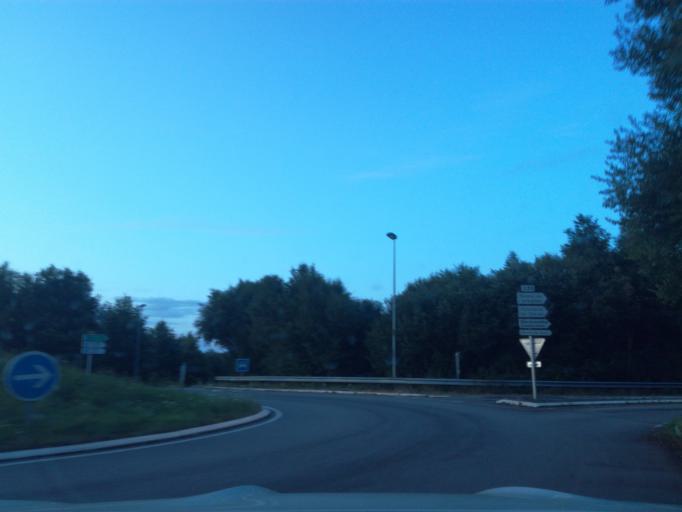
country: FR
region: Brittany
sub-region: Departement du Morbihan
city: Noyal-Pontivy
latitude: 48.0966
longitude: -2.9101
